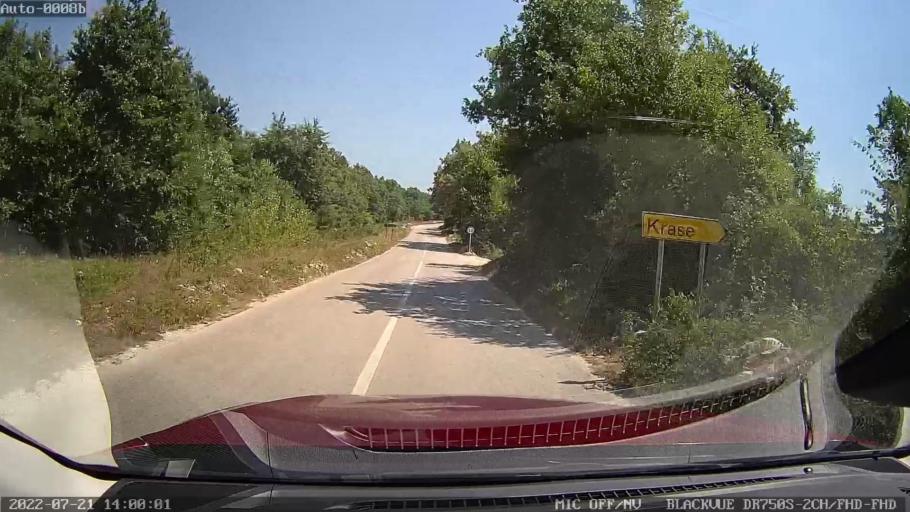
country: HR
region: Istarska
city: Vodnjan
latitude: 45.1010
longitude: 13.8665
